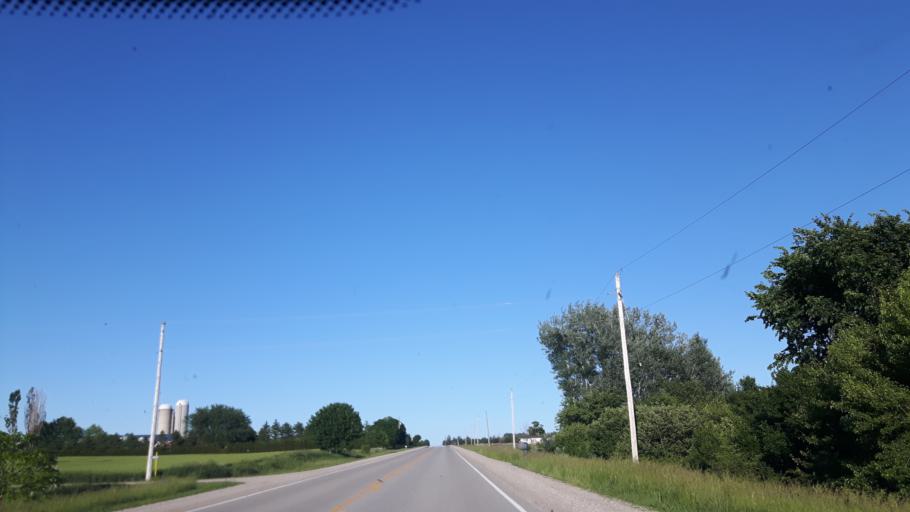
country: CA
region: Ontario
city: Goderich
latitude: 43.6428
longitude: -81.6565
